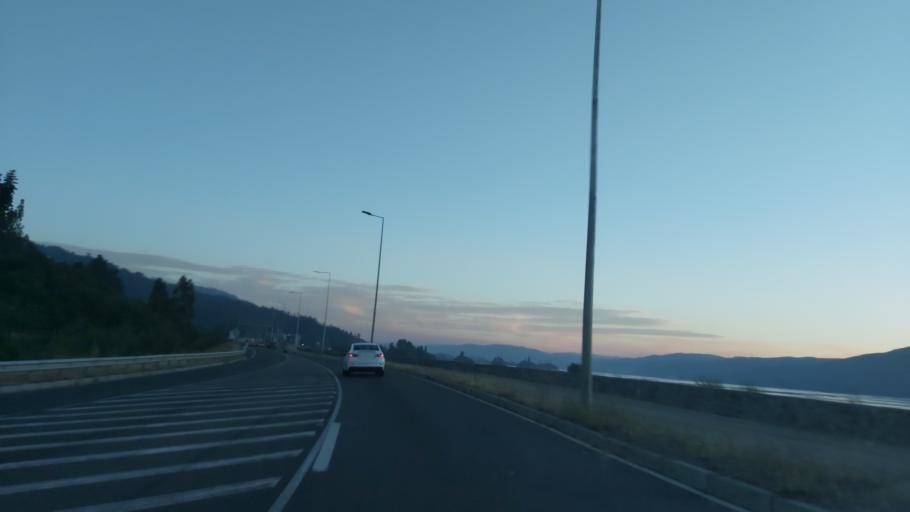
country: CL
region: Biobio
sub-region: Provincia de Concepcion
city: Concepcion
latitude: -36.8712
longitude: -73.0438
